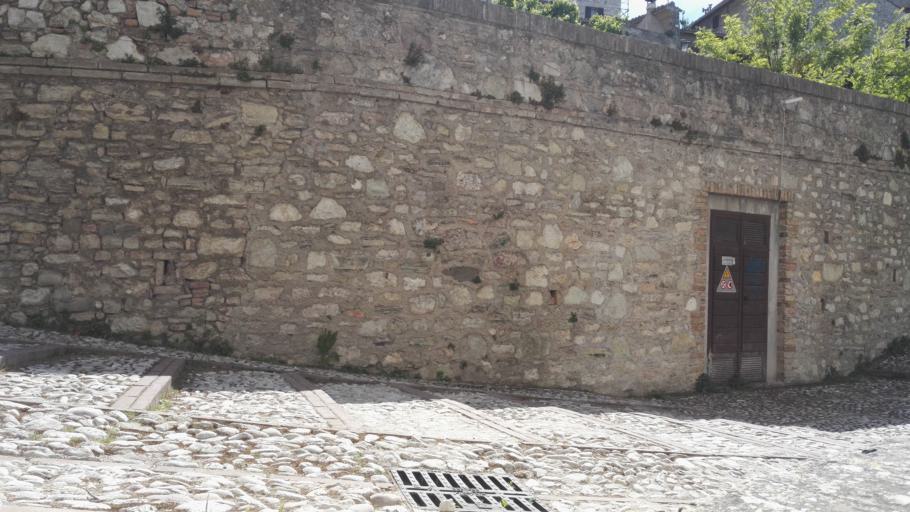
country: IT
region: Umbria
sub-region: Provincia di Perugia
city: Spoleto
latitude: 42.7370
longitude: 12.7372
